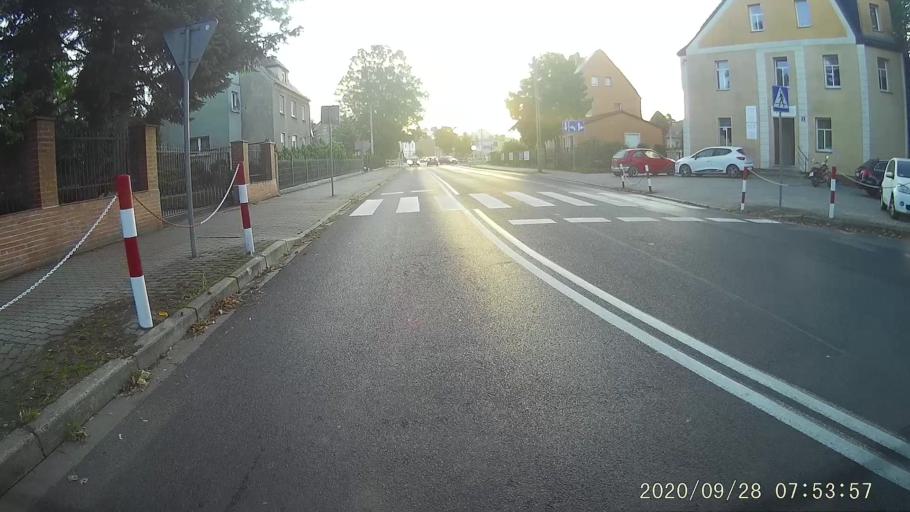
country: PL
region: Lower Silesian Voivodeship
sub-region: Powiat zgorzelecki
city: Bogatynia
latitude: 50.9130
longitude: 14.9633
